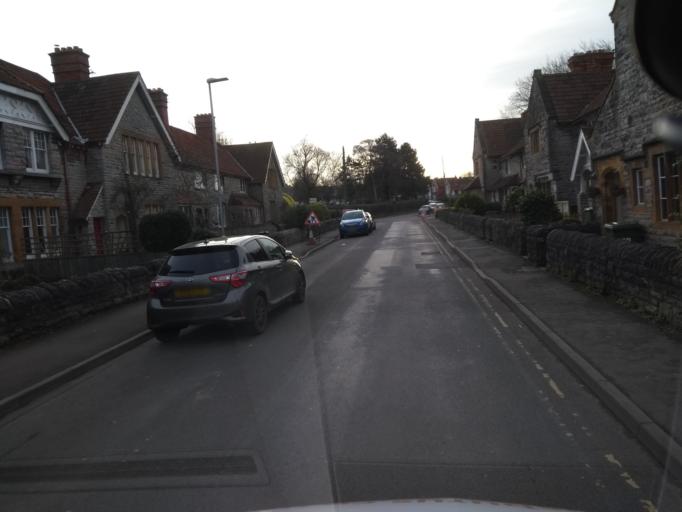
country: GB
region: England
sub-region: Somerset
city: Street
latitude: 51.1271
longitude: -2.7365
